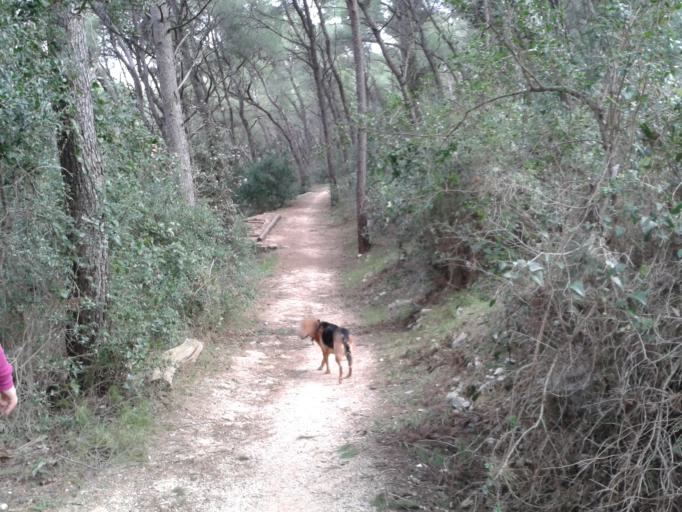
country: HR
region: Splitsko-Dalmatinska
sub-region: Grad Split
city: Split
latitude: 43.5116
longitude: 16.4040
